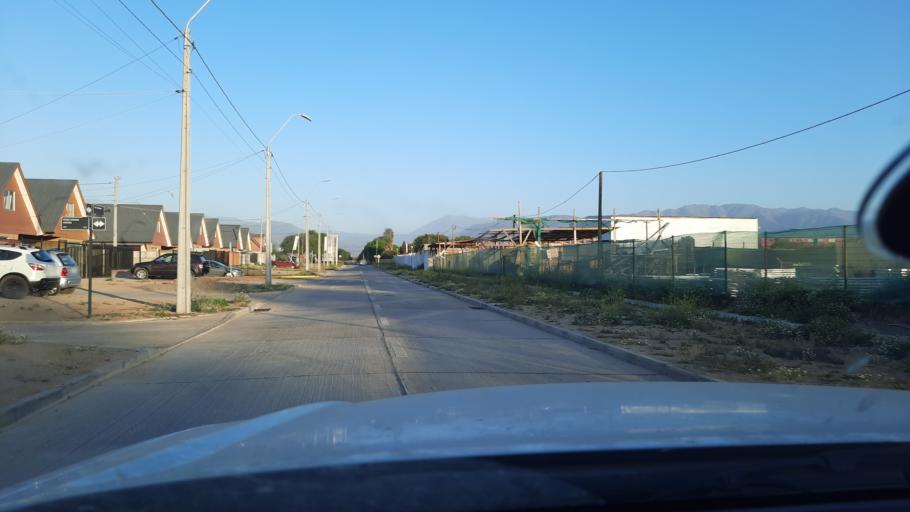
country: CL
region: Valparaiso
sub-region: Provincia de Marga Marga
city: Limache
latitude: -32.9965
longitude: -71.2778
